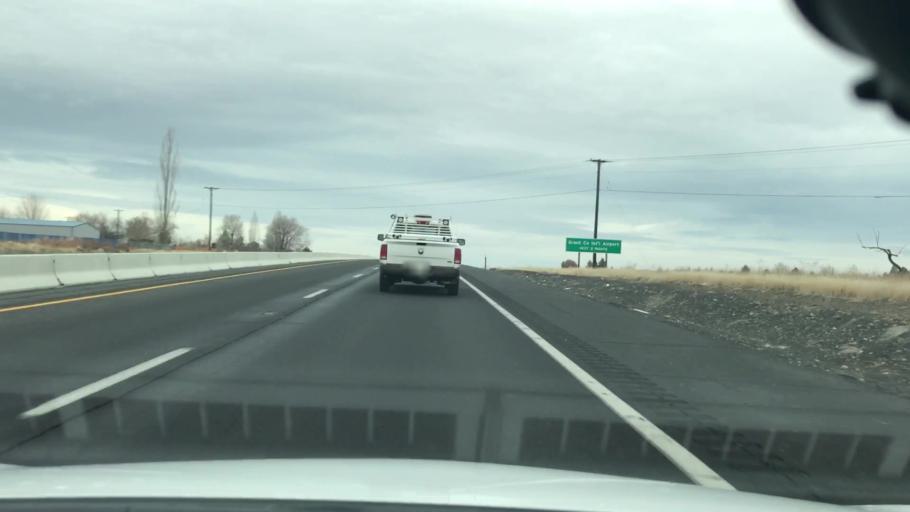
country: US
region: Washington
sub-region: Grant County
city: Cascade Valley
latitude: 47.1527
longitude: -119.3016
